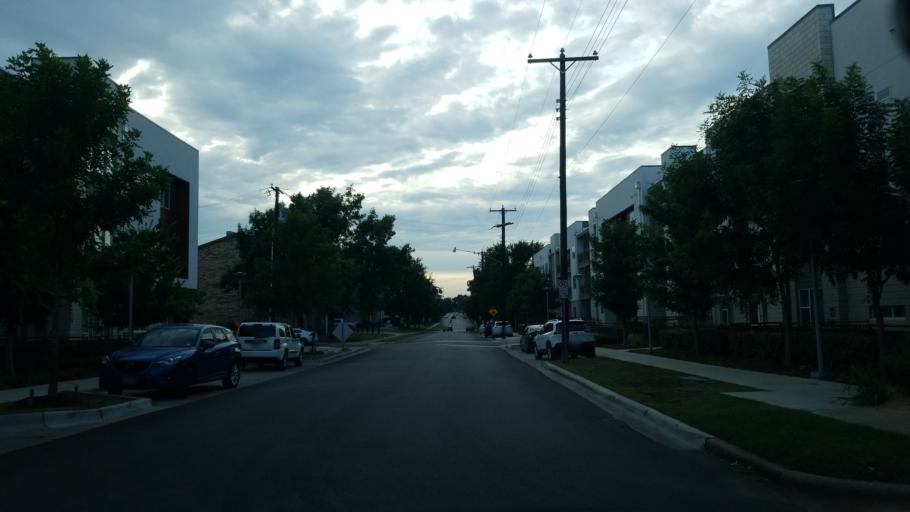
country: US
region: Texas
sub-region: Dallas County
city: Highland Park
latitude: 32.8101
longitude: -96.7768
